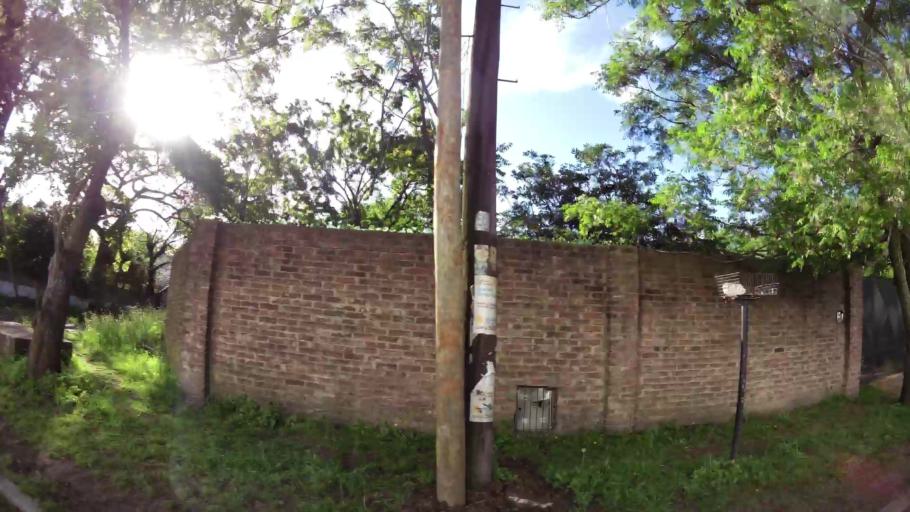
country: AR
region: Buenos Aires
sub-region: Partido de Quilmes
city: Quilmes
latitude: -34.8201
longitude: -58.2191
